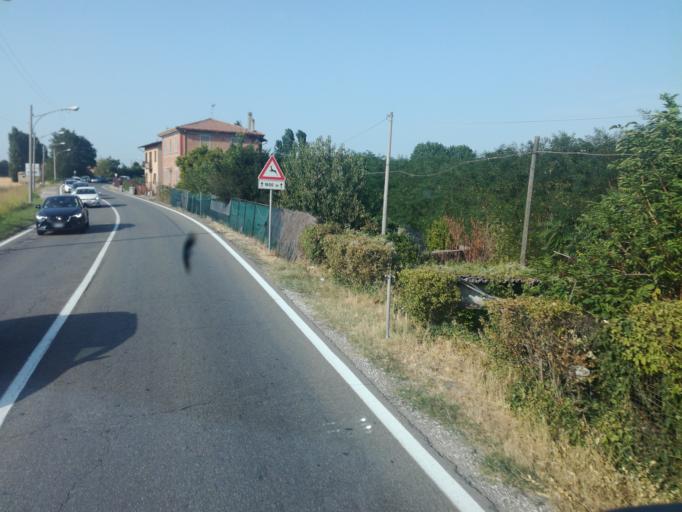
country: IT
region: Emilia-Romagna
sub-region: Provincia di Bologna
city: Progresso
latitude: 44.5421
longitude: 11.3726
